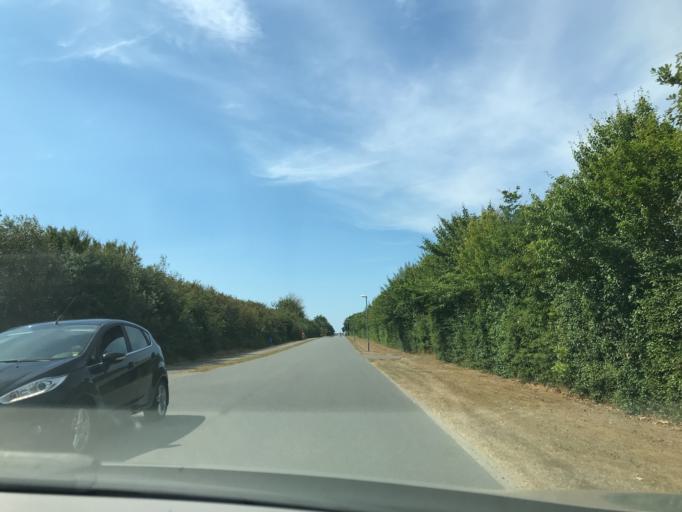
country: DK
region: Central Jutland
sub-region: Ringkobing-Skjern Kommune
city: Skjern
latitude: 55.8912
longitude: 8.3709
